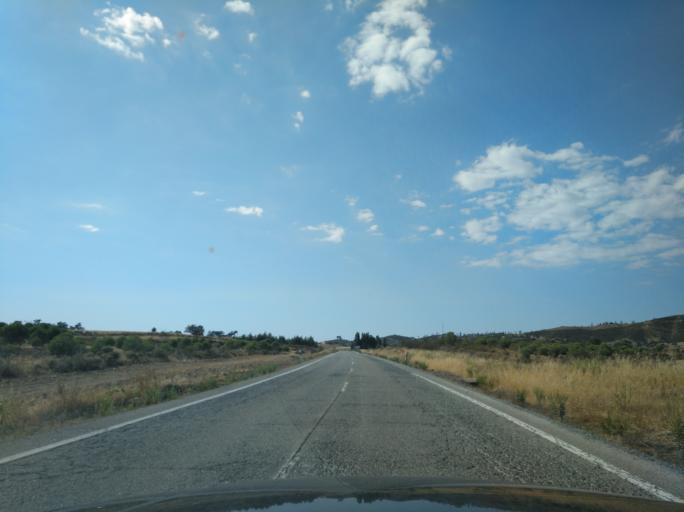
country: ES
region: Andalusia
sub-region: Provincia de Huelva
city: Santa Barbara de Casa
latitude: 37.7842
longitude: -7.1639
